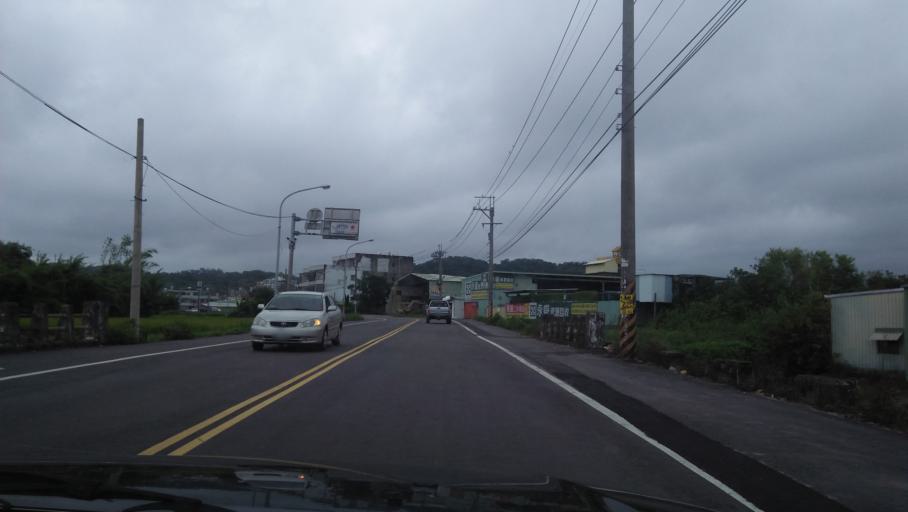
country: TW
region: Taiwan
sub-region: Hsinchu
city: Zhubei
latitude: 24.7881
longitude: 121.0646
